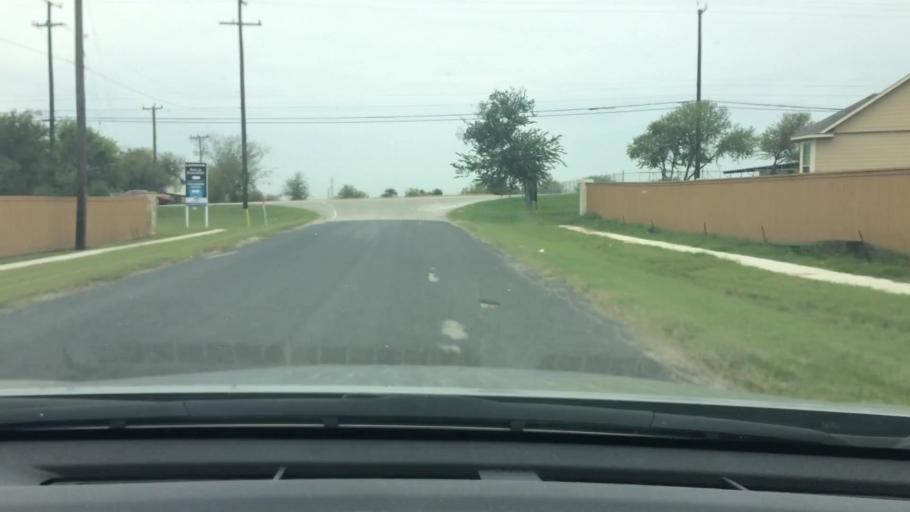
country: US
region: Texas
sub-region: Bexar County
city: Converse
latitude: 29.4705
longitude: -98.3127
